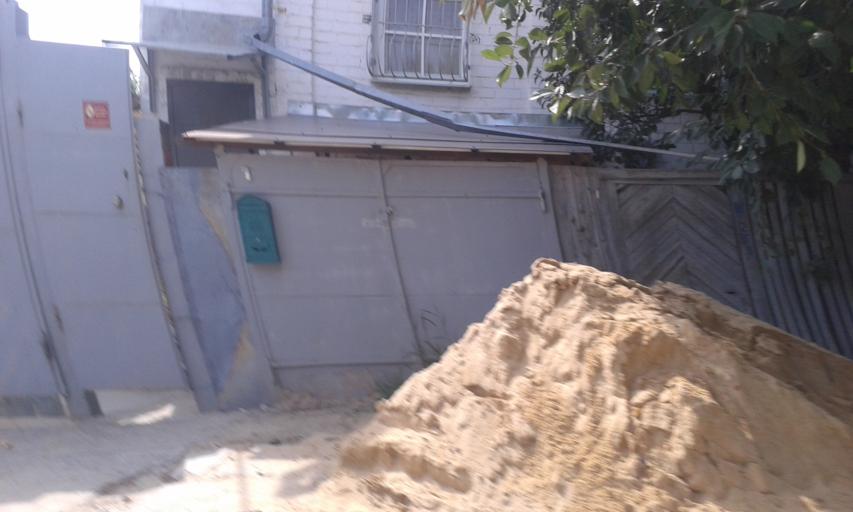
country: RU
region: Volgograd
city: Volgograd
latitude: 48.7597
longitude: 44.4845
